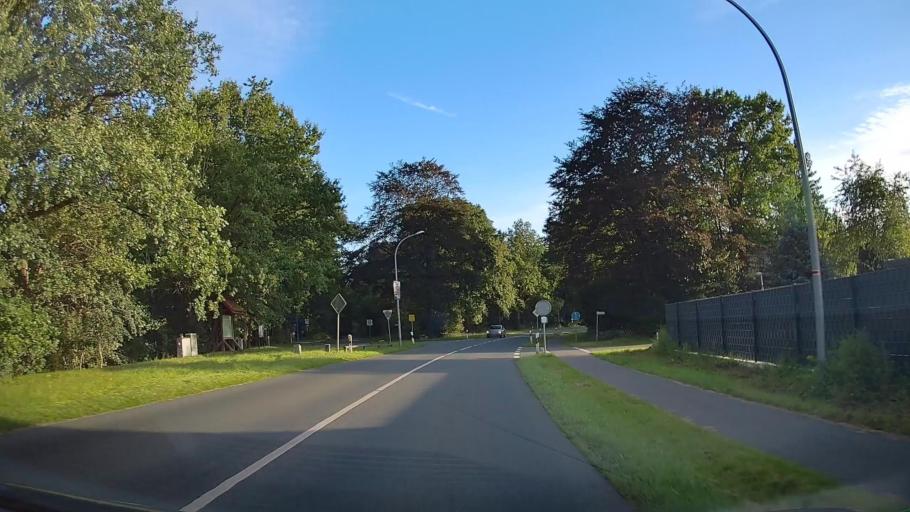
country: DE
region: Lower Saxony
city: Hellwege
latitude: 53.0884
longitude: 9.2375
